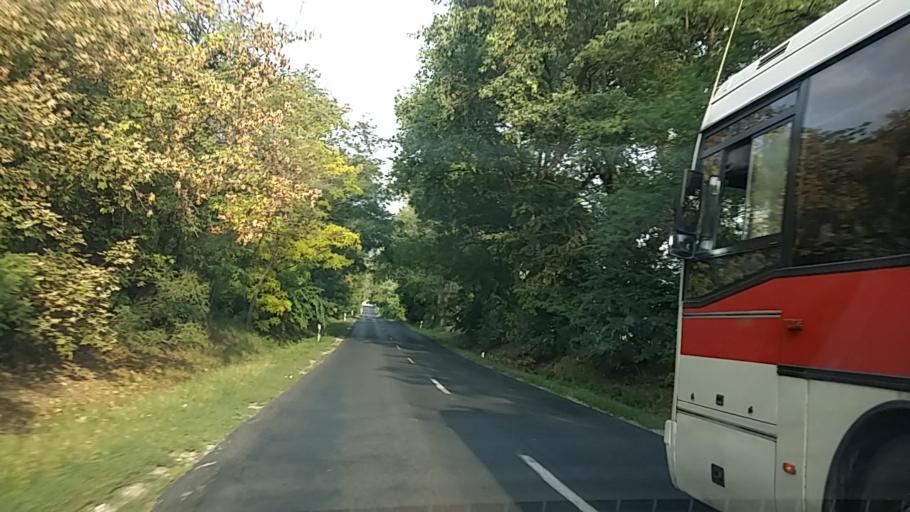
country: HU
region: Komarom-Esztergom
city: Kocs
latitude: 47.6264
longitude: 18.2541
